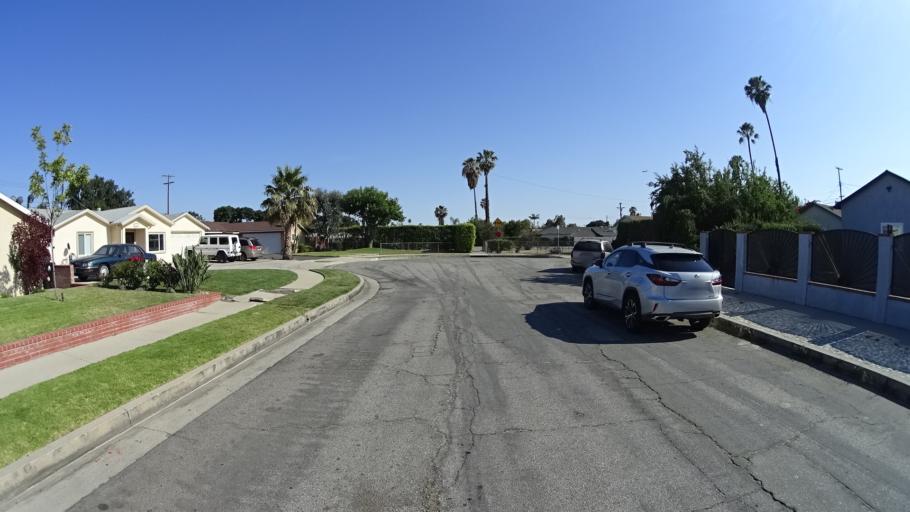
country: US
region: California
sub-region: Los Angeles County
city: Van Nuys
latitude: 34.2165
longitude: -118.4218
